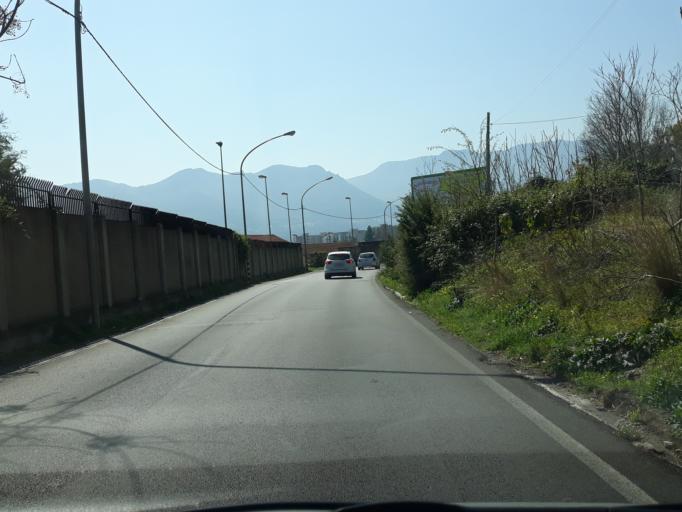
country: IT
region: Sicily
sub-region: Palermo
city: Monreale
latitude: 38.1026
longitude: 13.3104
